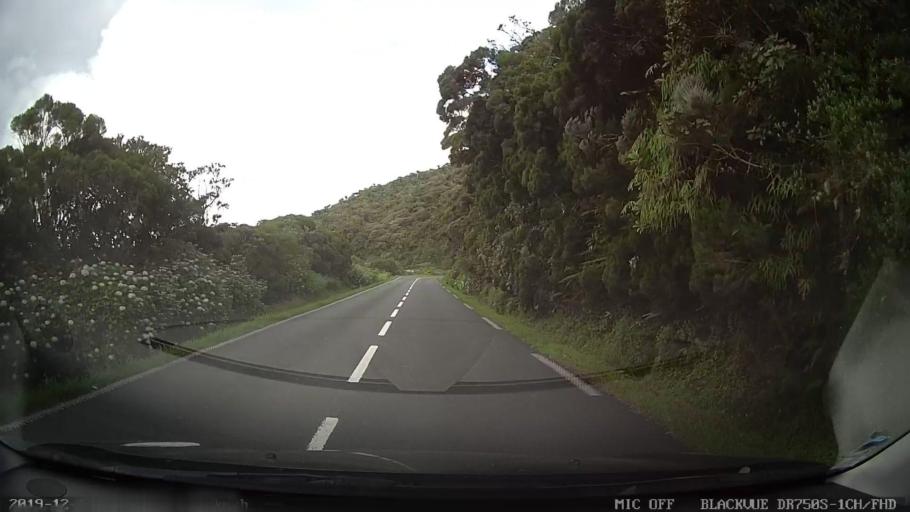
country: RE
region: Reunion
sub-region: Reunion
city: Cilaos
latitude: -21.1631
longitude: 55.5949
